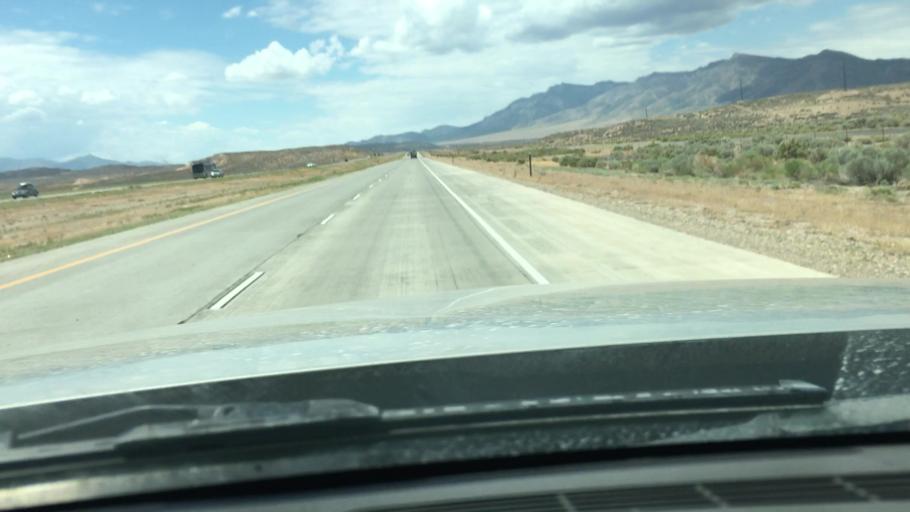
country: US
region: Utah
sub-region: Sanpete County
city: Gunnison
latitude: 39.4067
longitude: -112.0549
